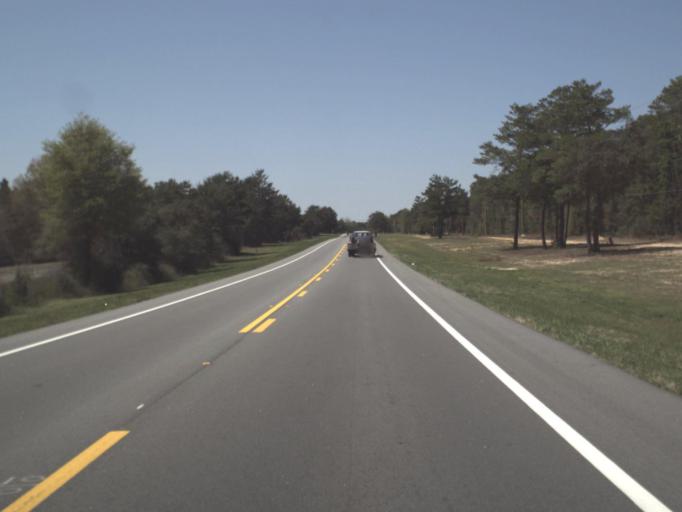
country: US
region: Florida
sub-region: Walton County
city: DeFuniak Springs
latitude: 30.7458
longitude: -86.3048
